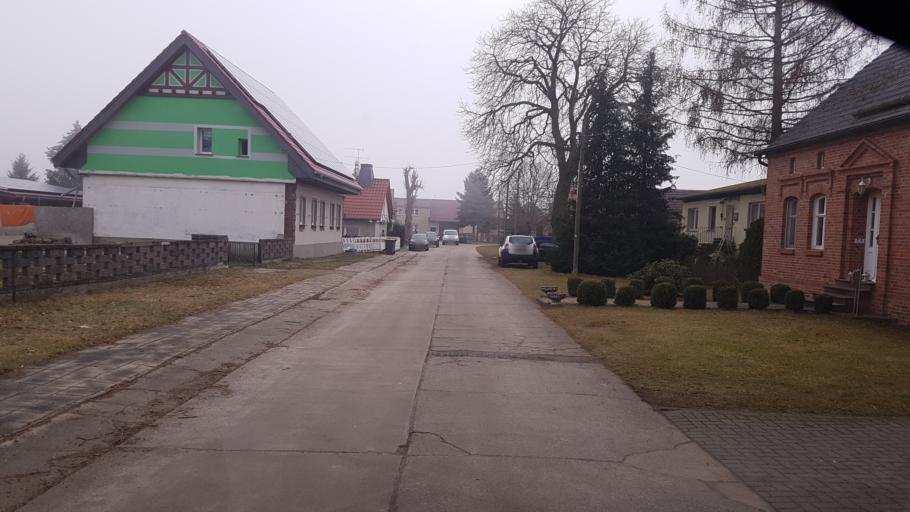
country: DE
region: Saxony-Anhalt
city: Holzdorf
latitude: 51.8616
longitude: 13.2135
